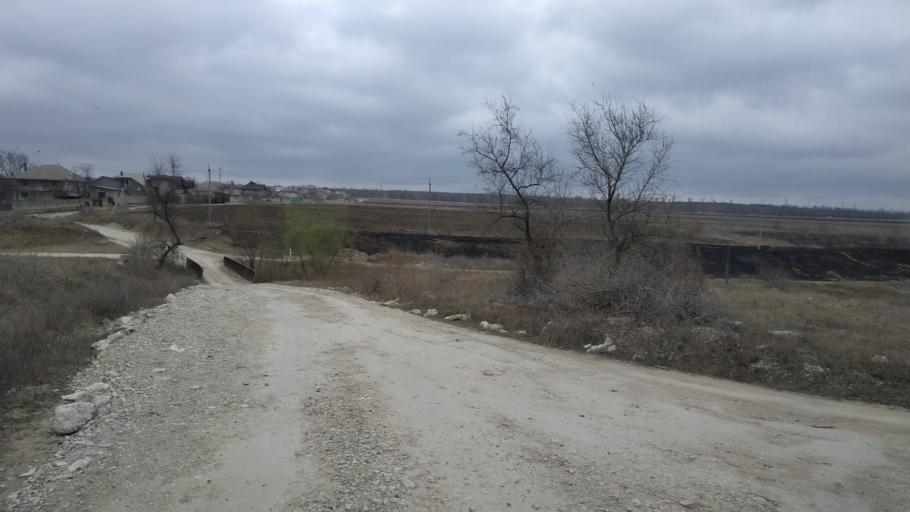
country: MD
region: Laloveni
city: Ialoveni
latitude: 46.9319
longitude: 28.7947
